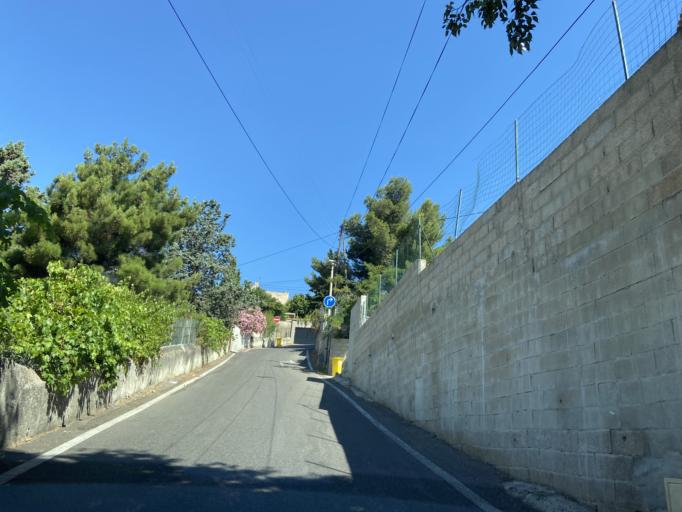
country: FR
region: Provence-Alpes-Cote d'Azur
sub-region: Departement des Bouches-du-Rhone
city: Marseille 15
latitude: 43.3732
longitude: 5.3442
